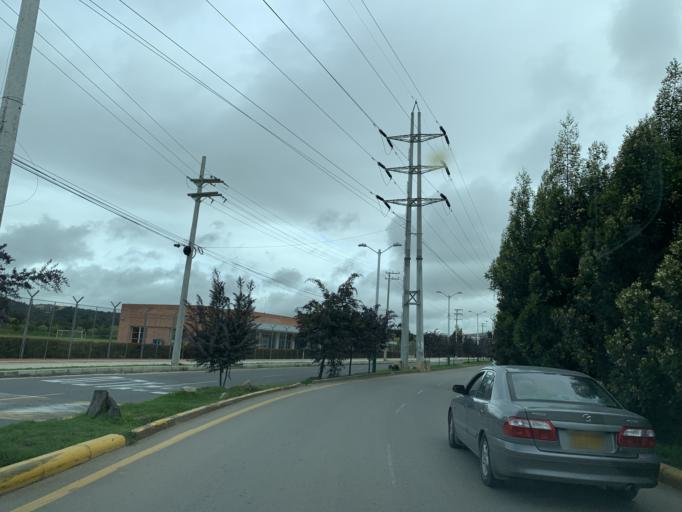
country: CO
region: Boyaca
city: Tunja
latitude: 5.5687
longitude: -73.3323
